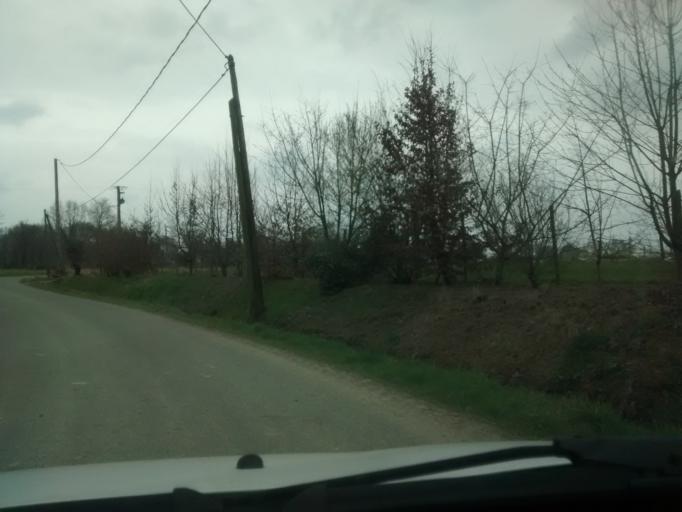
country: FR
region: Brittany
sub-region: Departement d'Ille-et-Vilaine
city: Sens-de-Bretagne
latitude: 48.3860
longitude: -1.5321
